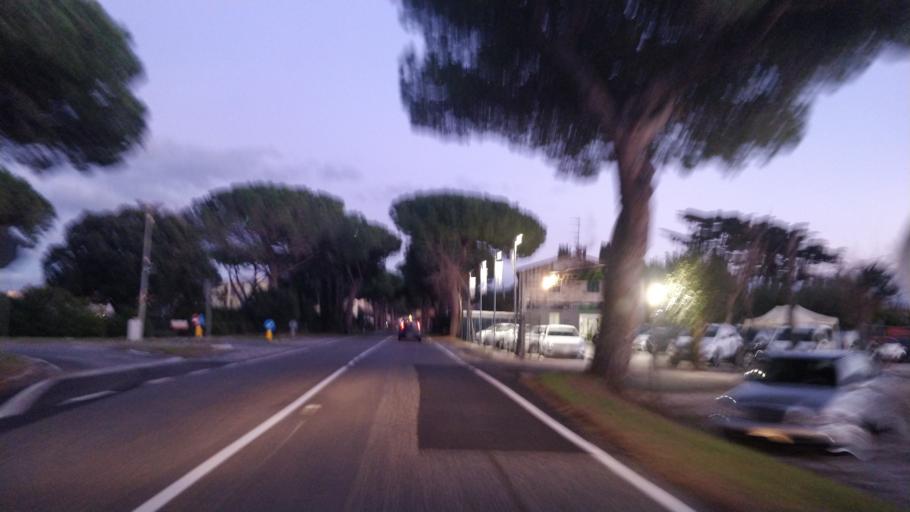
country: IT
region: Tuscany
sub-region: Provincia di Livorno
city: S.P. in Palazzi
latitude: 43.3309
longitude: 10.4995
